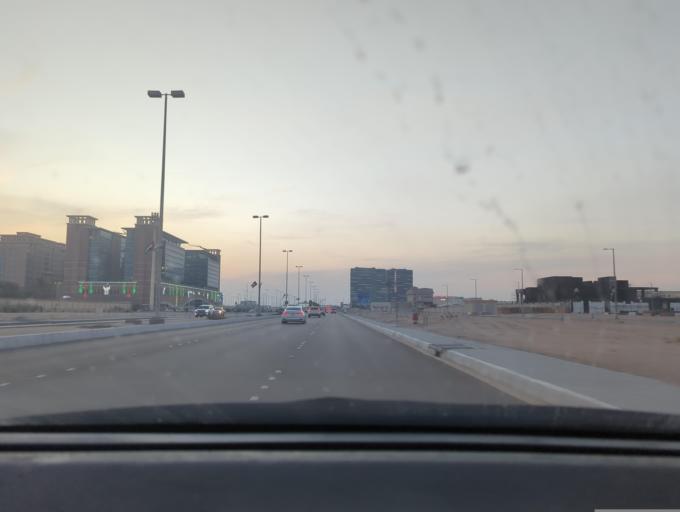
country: AE
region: Abu Dhabi
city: Abu Dhabi
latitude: 24.3746
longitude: 54.5423
